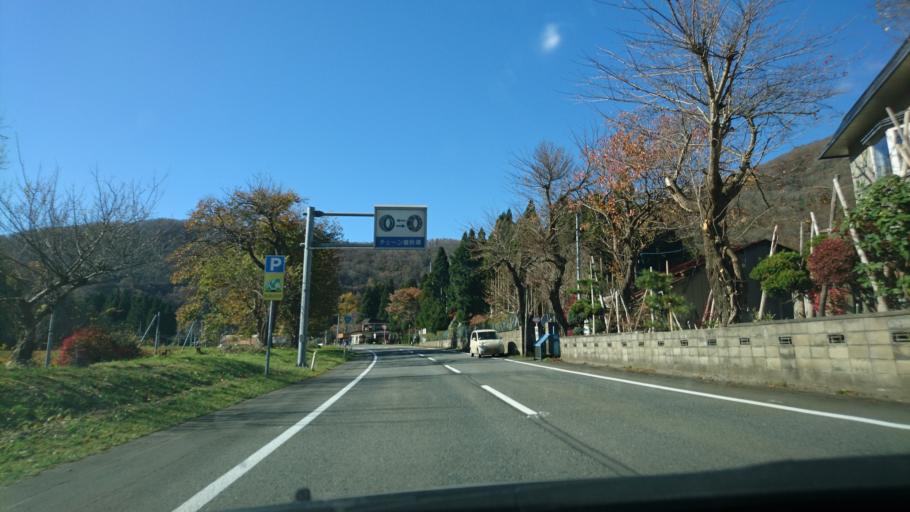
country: JP
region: Iwate
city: Kitakami
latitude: 39.3095
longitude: 140.9054
